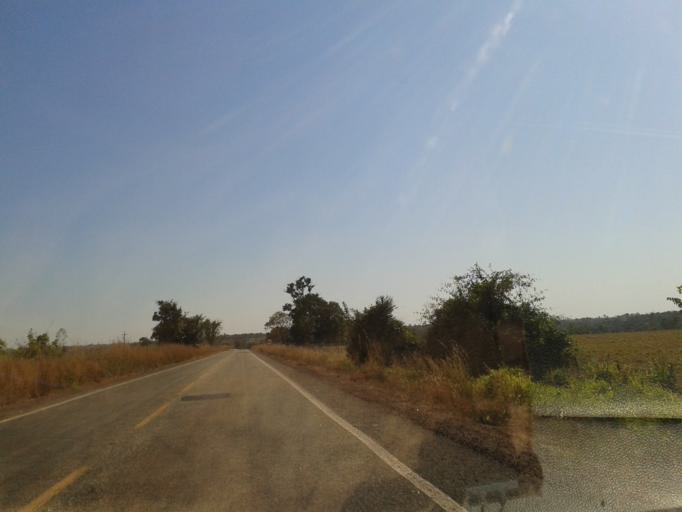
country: BR
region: Goias
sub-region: Mozarlandia
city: Mozarlandia
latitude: -14.4997
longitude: -50.4846
